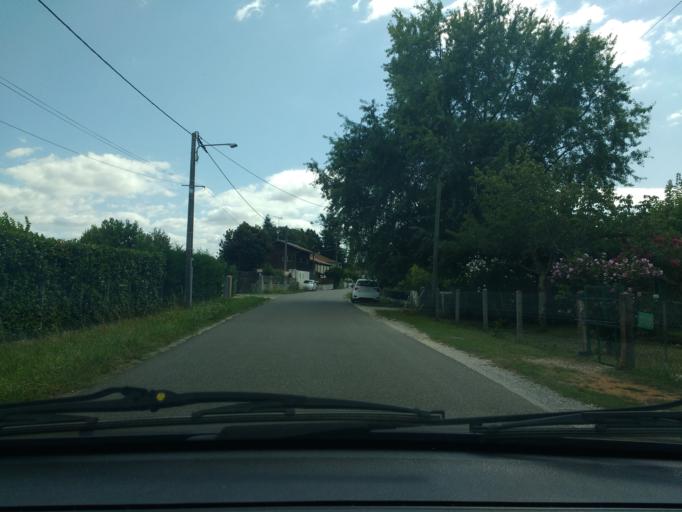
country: FR
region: Aquitaine
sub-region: Departement de la Gironde
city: Salles
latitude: 44.5575
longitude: -0.8565
